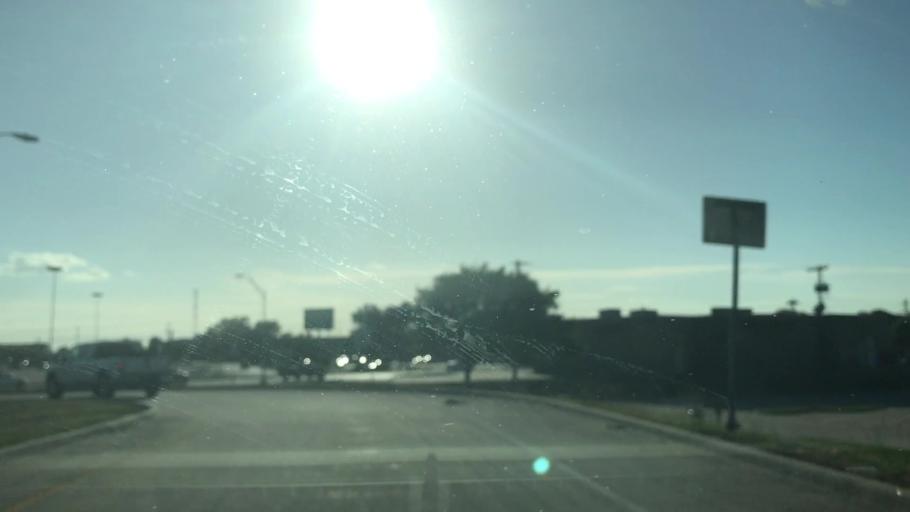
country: US
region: Texas
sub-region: Collin County
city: Plano
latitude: 33.0382
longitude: -96.7059
